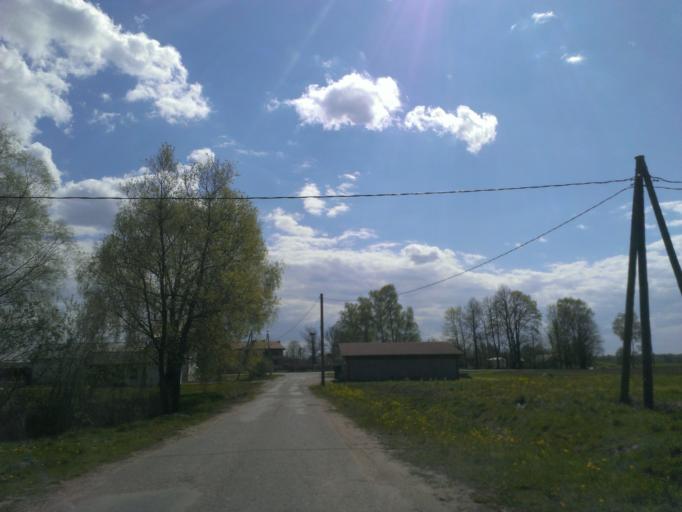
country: LV
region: Saulkrastu
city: Saulkrasti
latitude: 57.3309
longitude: 24.4895
